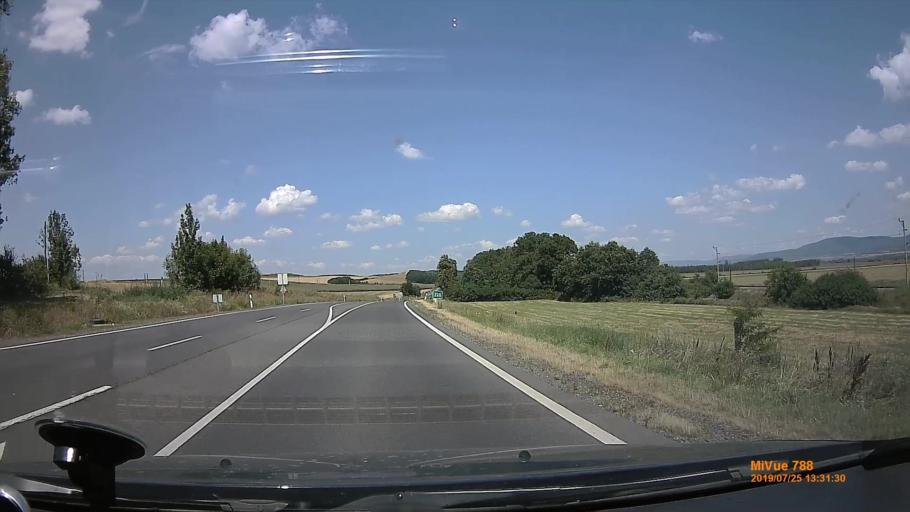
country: HU
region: Borsod-Abauj-Zemplen
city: Encs
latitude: 48.3641
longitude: 21.1400
